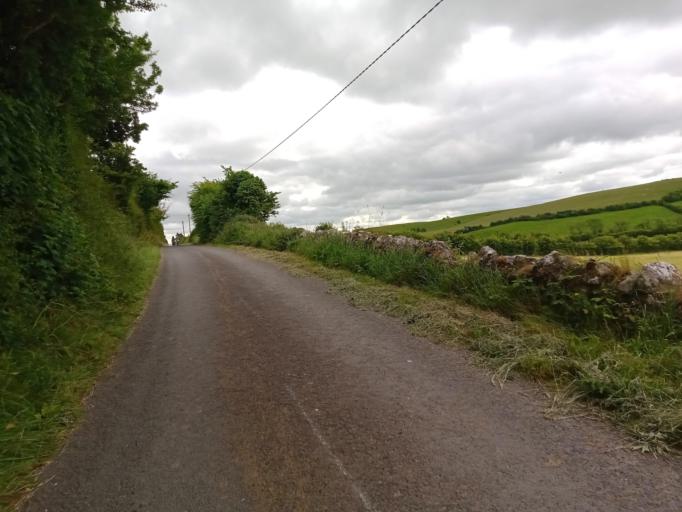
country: IE
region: Leinster
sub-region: Laois
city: Rathdowney
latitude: 52.7868
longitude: -7.4792
